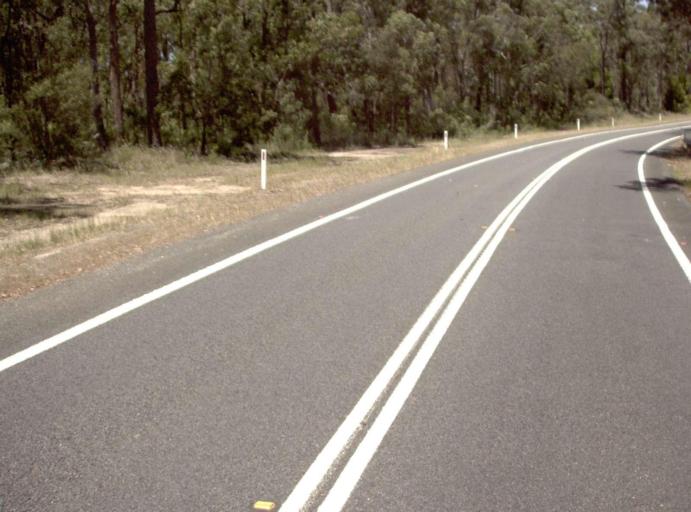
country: AU
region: Victoria
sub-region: East Gippsland
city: Lakes Entrance
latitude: -37.8259
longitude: 148.0335
